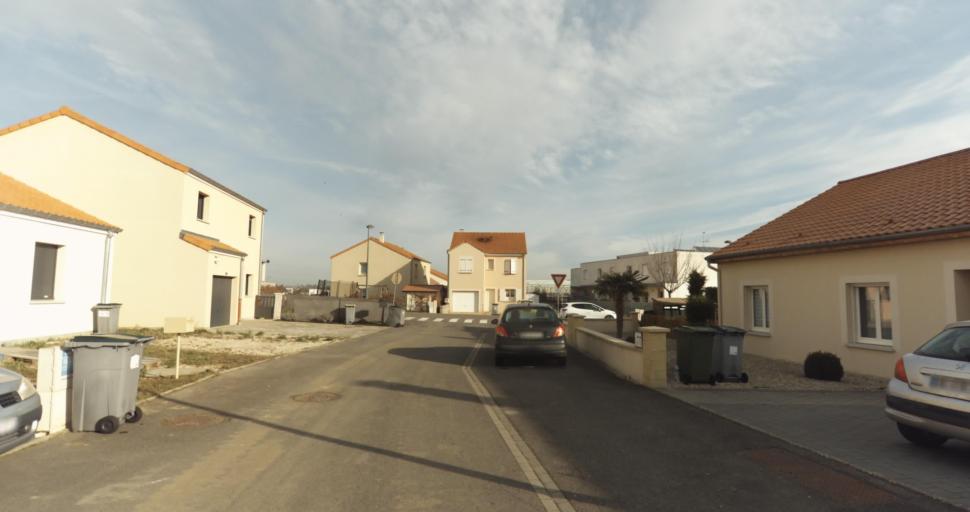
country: FR
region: Lorraine
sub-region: Departement de Meurthe-et-Moselle
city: Jarny
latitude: 49.1589
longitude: 5.8848
